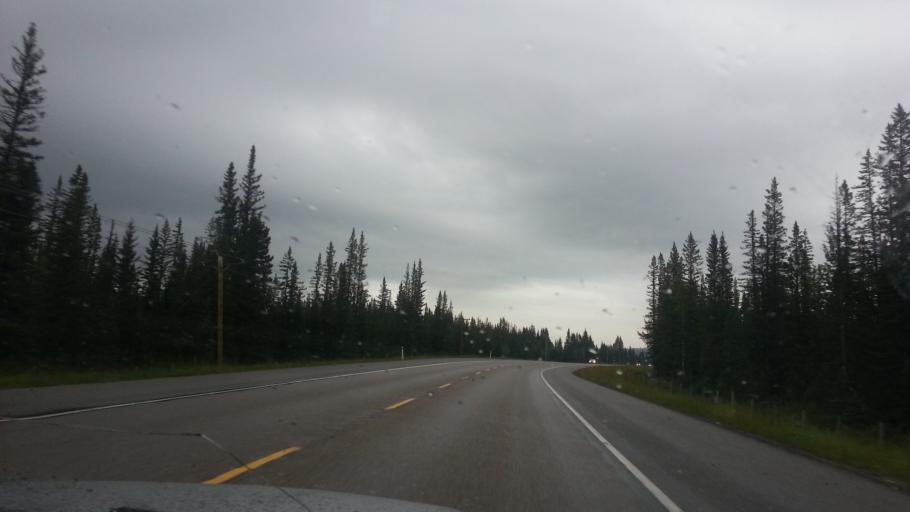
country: CA
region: Alberta
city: Cochrane
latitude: 50.9703
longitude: -114.5364
